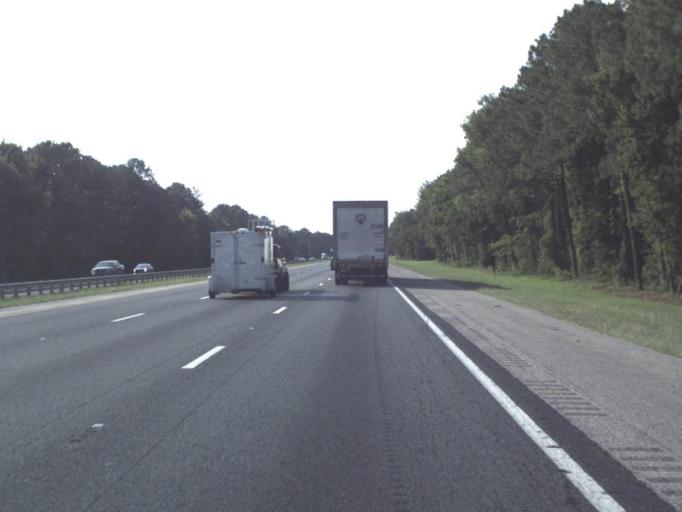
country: US
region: Florida
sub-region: Saint Johns County
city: Fruit Cove
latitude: 30.0367
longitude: -81.4923
